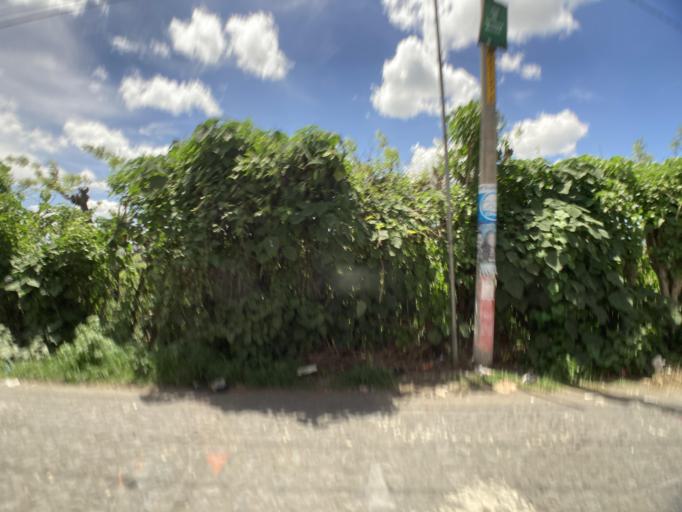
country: GT
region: Sacatepequez
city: Ciudad Vieja
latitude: 14.5283
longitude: -90.7443
